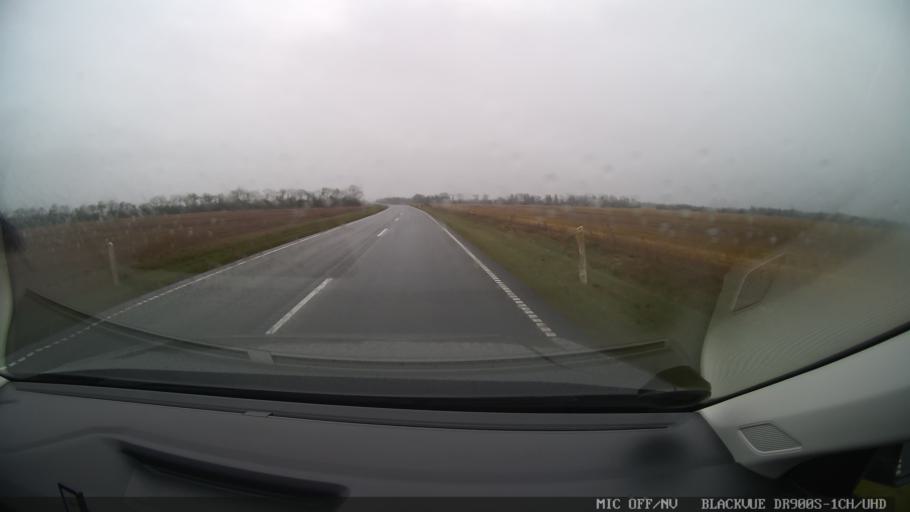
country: DK
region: Central Jutland
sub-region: Herning Kommune
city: Sunds
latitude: 56.2793
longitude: 8.9510
